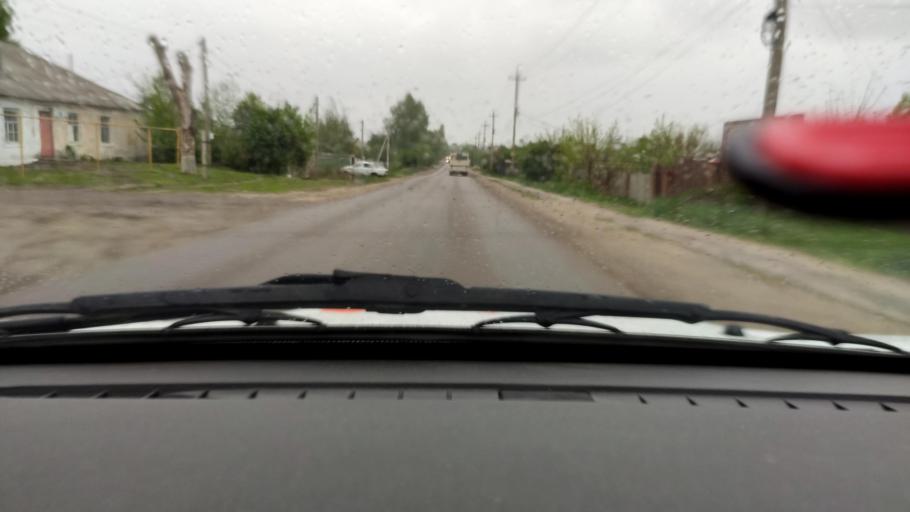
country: RU
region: Voronezj
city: Strelitsa
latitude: 51.6231
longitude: 38.9138
